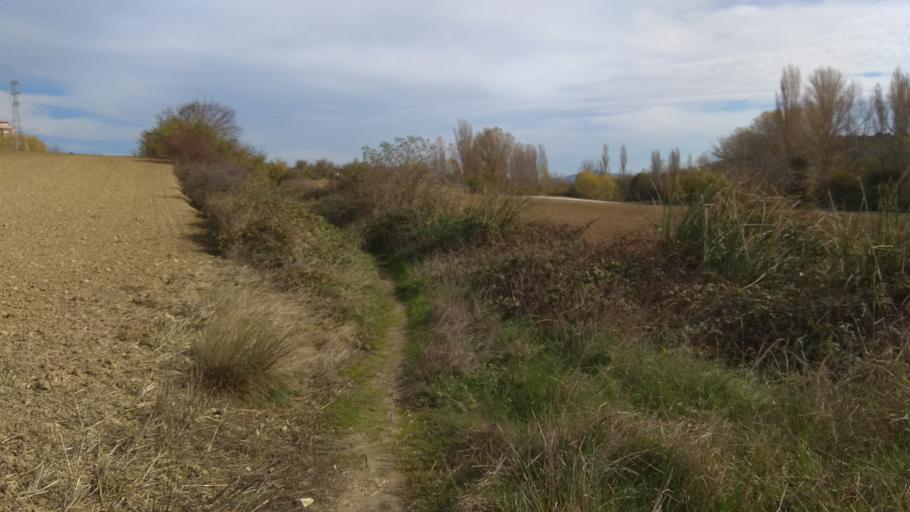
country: ES
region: Navarre
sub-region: Provincia de Navarra
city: Cizur Mayor
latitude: 42.7991
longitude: -1.6958
